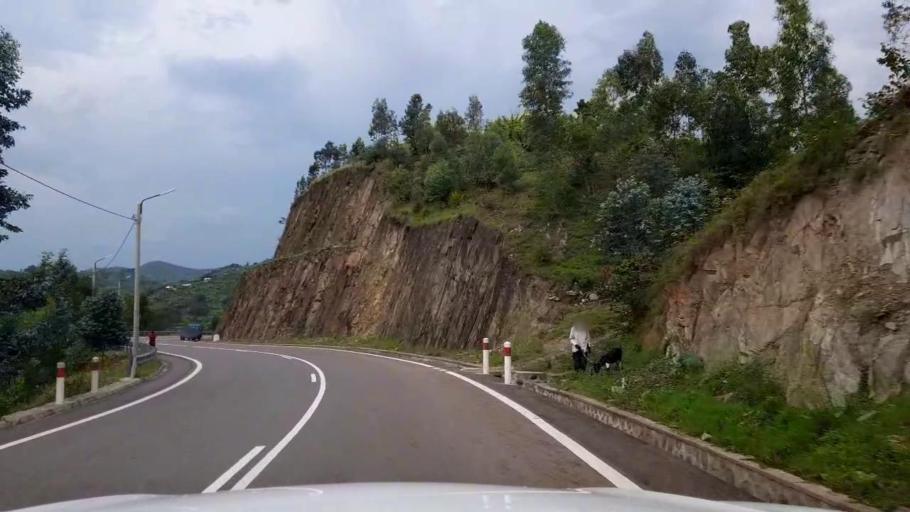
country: RW
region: Western Province
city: Kibuye
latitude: -2.0361
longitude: 29.3987
